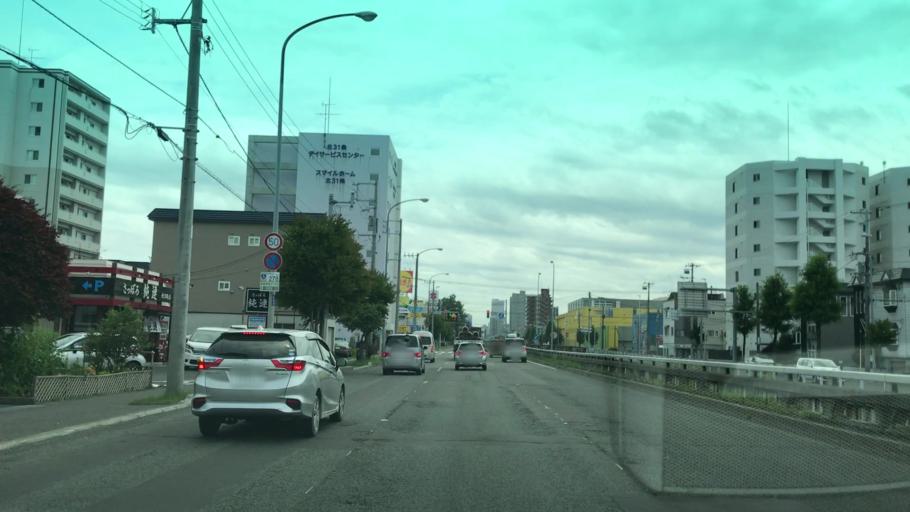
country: JP
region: Hokkaido
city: Sapporo
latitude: 43.0991
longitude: 141.3456
